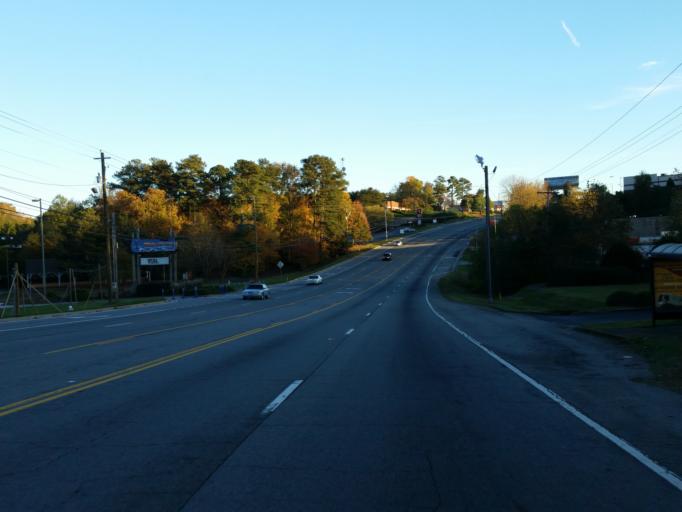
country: US
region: Georgia
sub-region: Cobb County
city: Marietta
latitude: 33.9574
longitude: -84.5249
